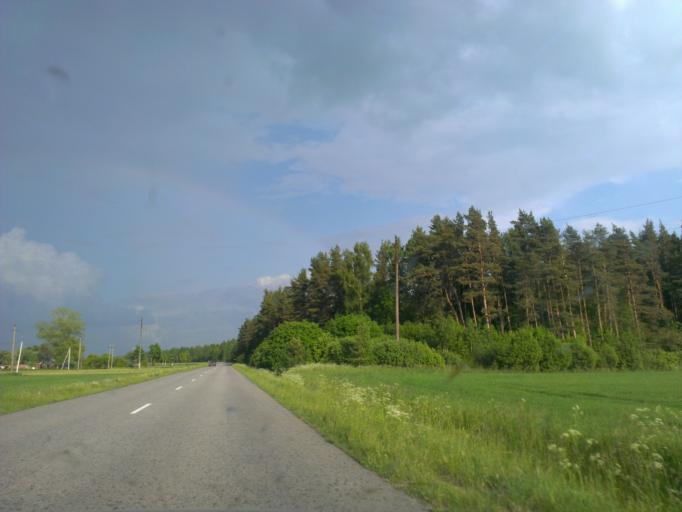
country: LT
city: Salantai
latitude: 56.0645
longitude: 21.4311
